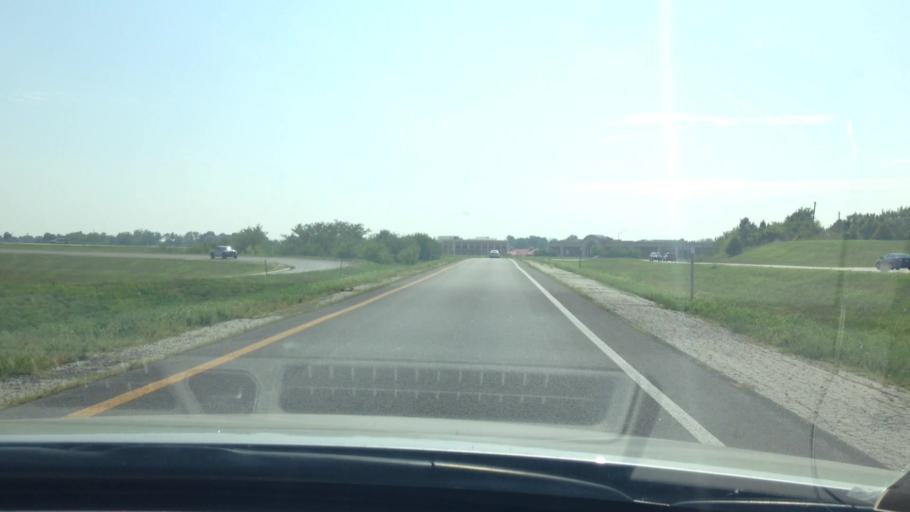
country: US
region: Missouri
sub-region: Platte County
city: Weatherby Lake
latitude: 39.2569
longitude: -94.6604
